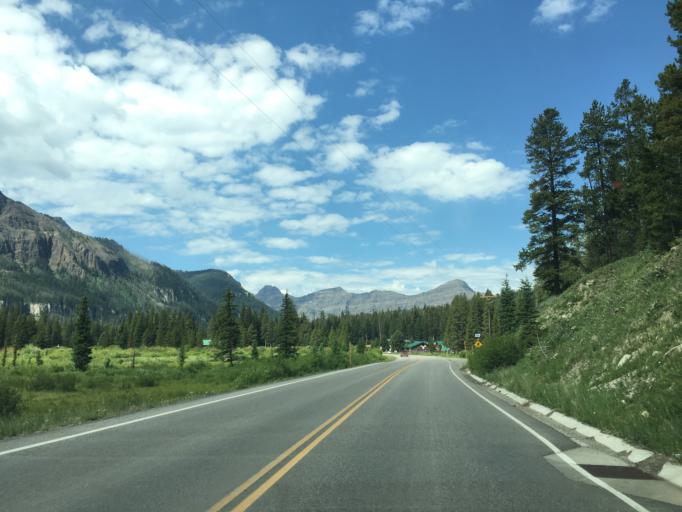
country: US
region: Montana
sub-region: Stillwater County
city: Absarokee
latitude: 45.0081
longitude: -109.9851
